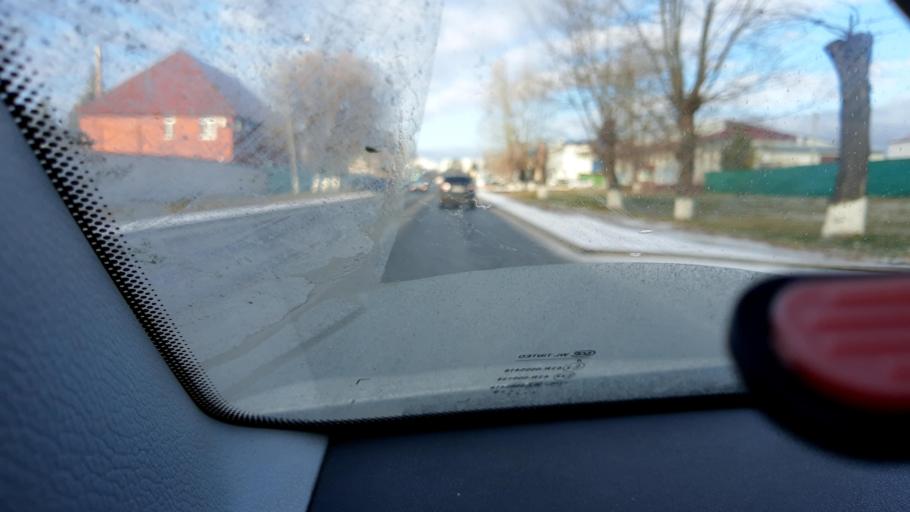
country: RU
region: Bashkortostan
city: Ufa
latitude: 54.8055
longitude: 56.0898
